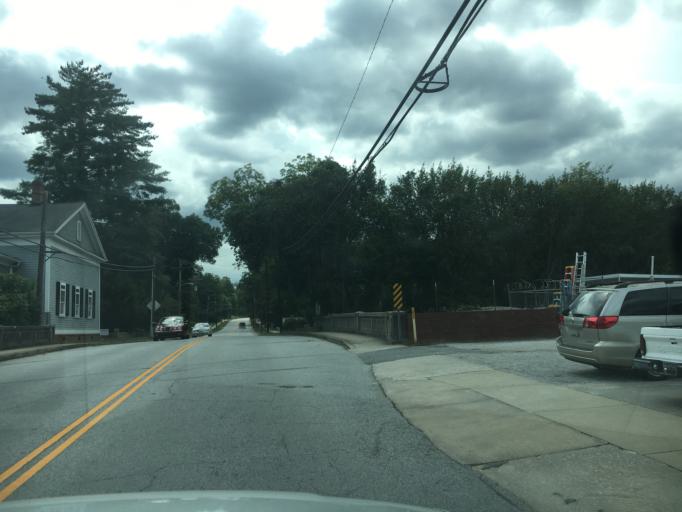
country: US
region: South Carolina
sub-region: Laurens County
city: Laurens
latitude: 34.4977
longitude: -82.0200
